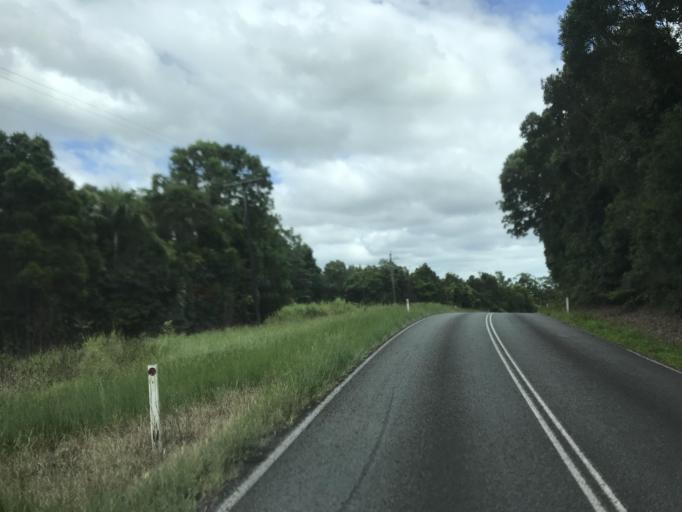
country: AU
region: Queensland
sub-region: Cassowary Coast
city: Innisfail
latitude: -17.8372
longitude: 146.0523
